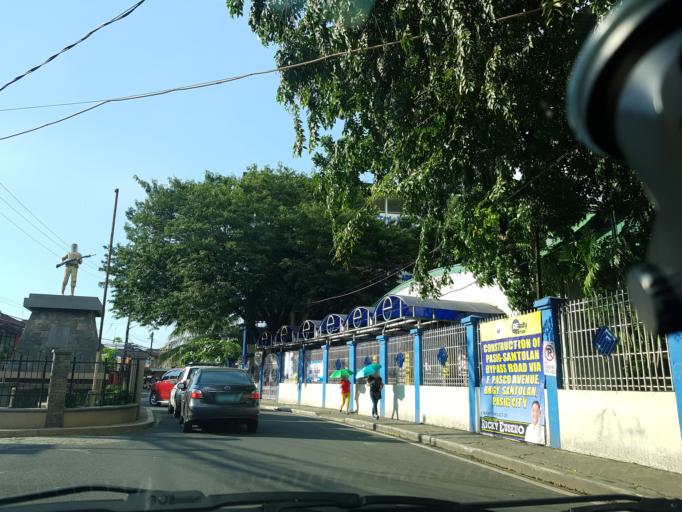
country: PH
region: Metro Manila
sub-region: Marikina
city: Calumpang
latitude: 14.6148
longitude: 121.0820
